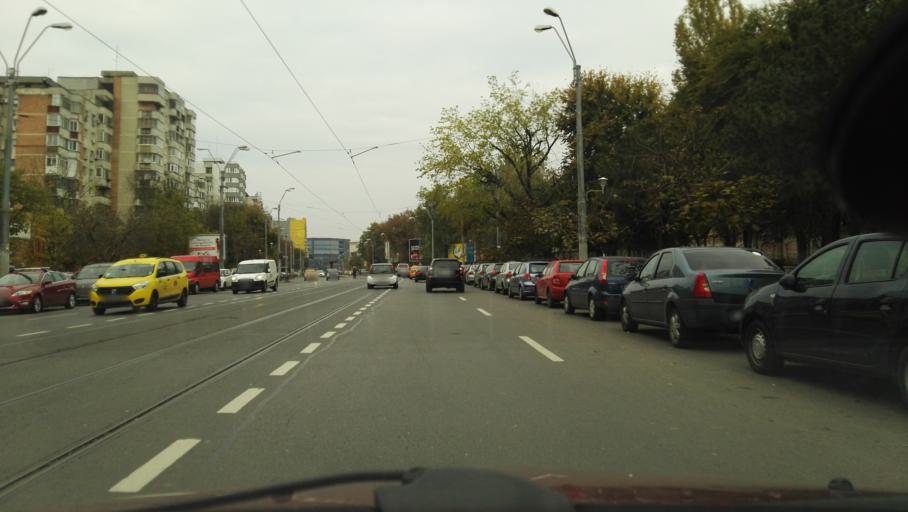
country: RO
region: Bucuresti
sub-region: Municipiul Bucuresti
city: Bucuresti
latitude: 44.3994
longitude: 26.1069
